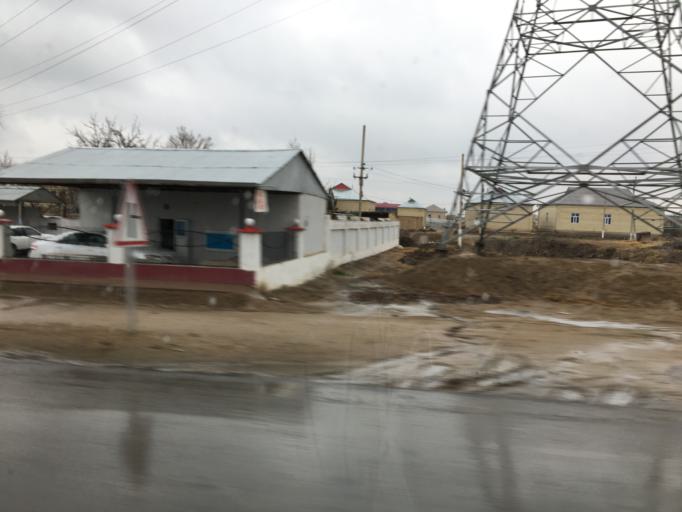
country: TM
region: Mary
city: Mary
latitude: 37.5366
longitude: 61.8837
